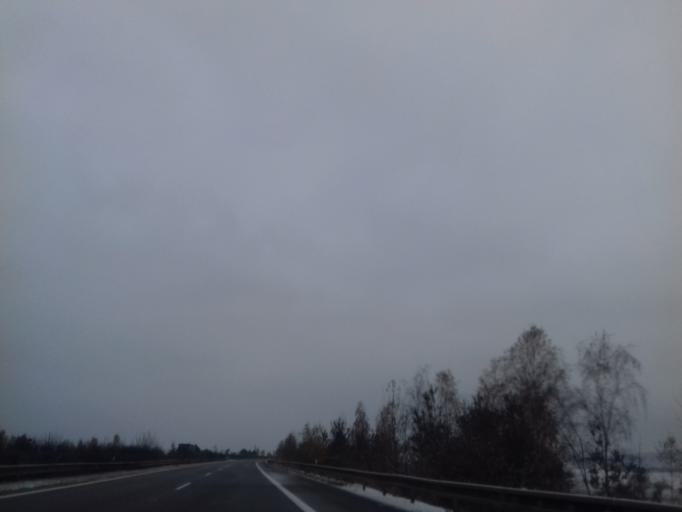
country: CZ
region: Plzensky
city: Zbiroh
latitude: 49.8288
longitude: 13.7786
